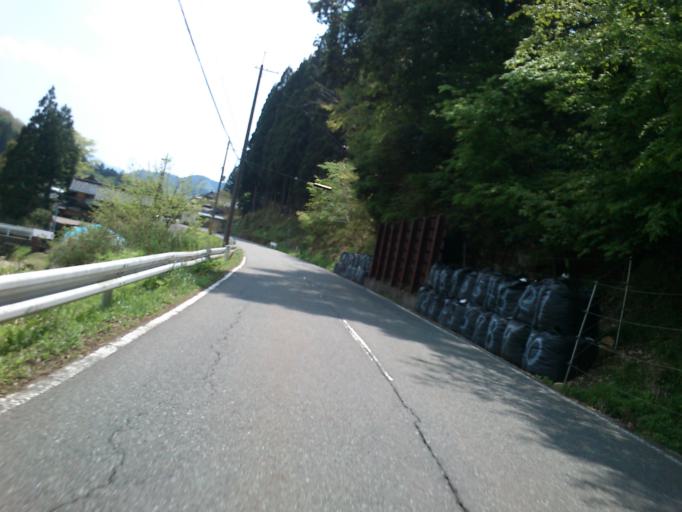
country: JP
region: Hyogo
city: Toyooka
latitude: 35.3947
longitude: 134.9439
